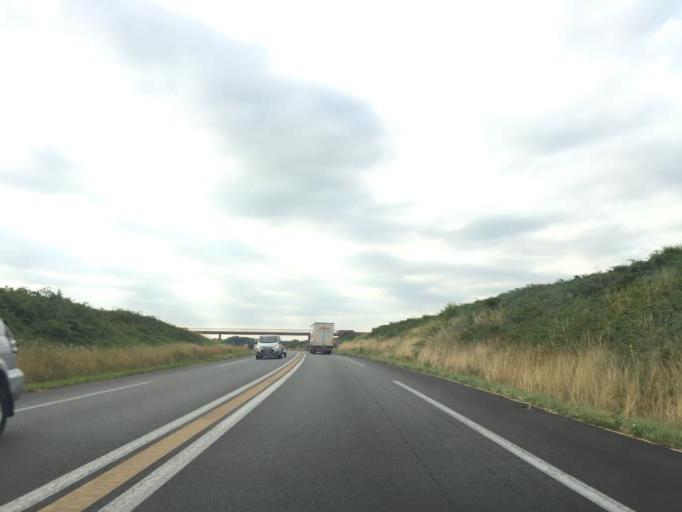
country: FR
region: Auvergne
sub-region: Departement de l'Allier
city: Diou
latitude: 46.5040
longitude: 3.7810
